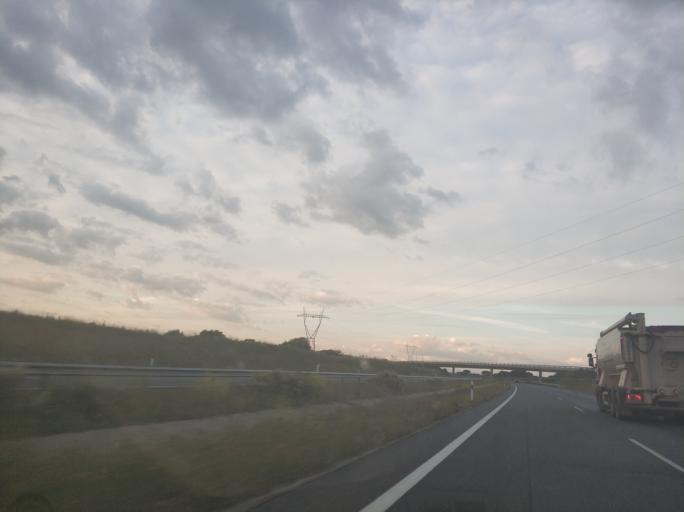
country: ES
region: Castille and Leon
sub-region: Provincia de Salamanca
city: Montejo
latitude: 40.6548
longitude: -5.6273
